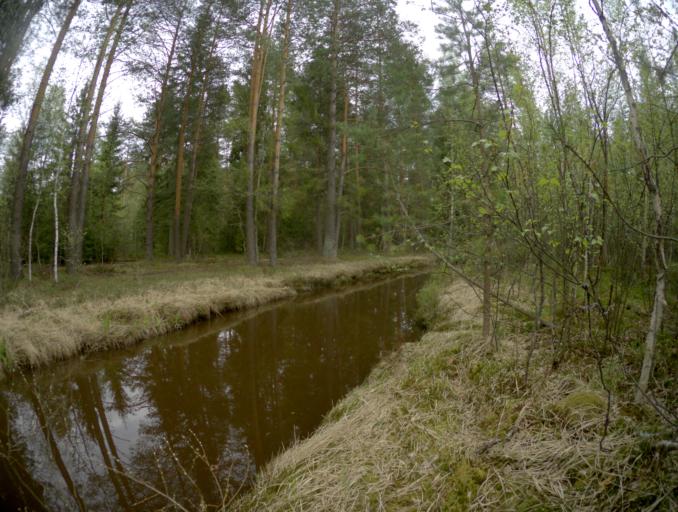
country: RU
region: Vladimir
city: Golovino
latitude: 55.9193
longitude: 40.4099
